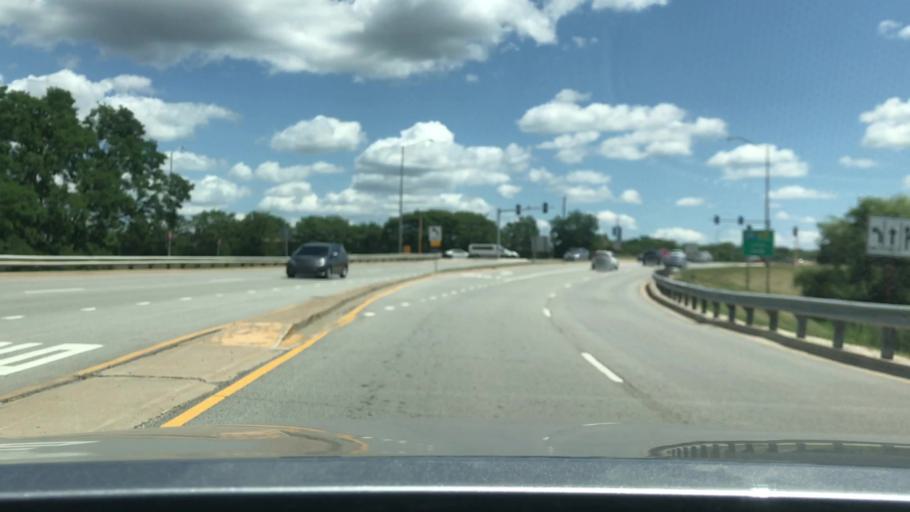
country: US
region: Illinois
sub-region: DuPage County
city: Woodridge
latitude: 41.7718
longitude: -88.0480
